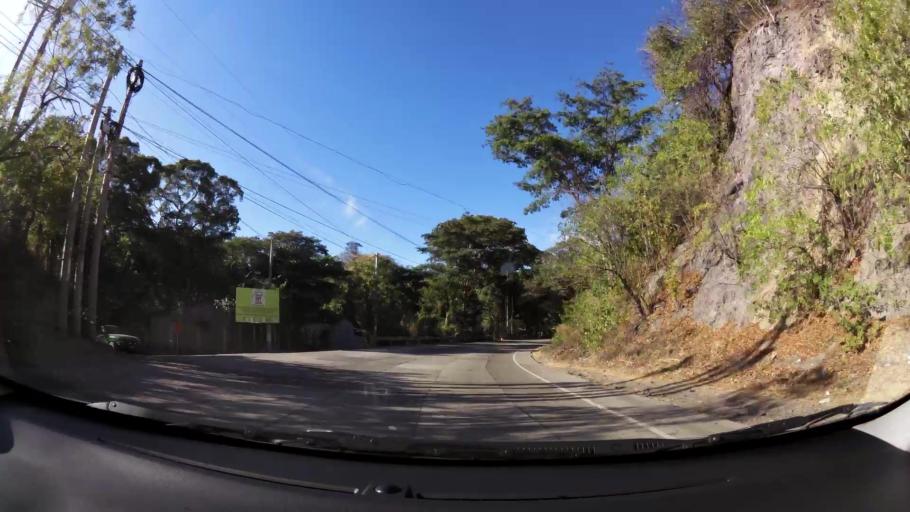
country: SV
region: Santa Ana
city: Texistepeque
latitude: 14.1401
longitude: -89.5136
